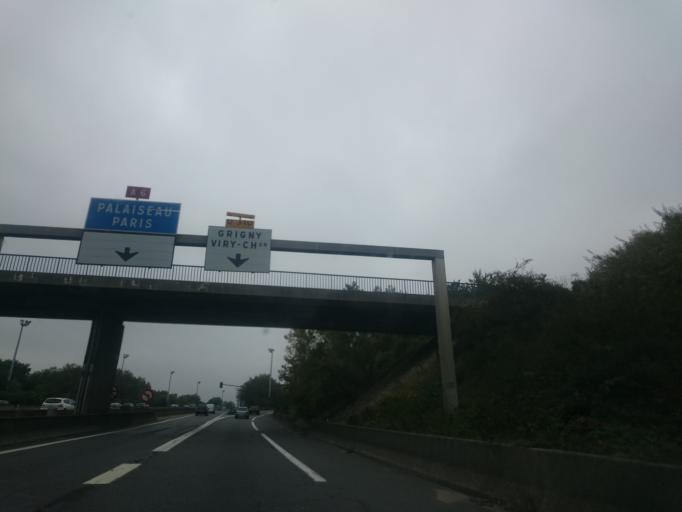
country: FR
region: Ile-de-France
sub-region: Departement de l'Essonne
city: Grigny
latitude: 48.6389
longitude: 2.3963
